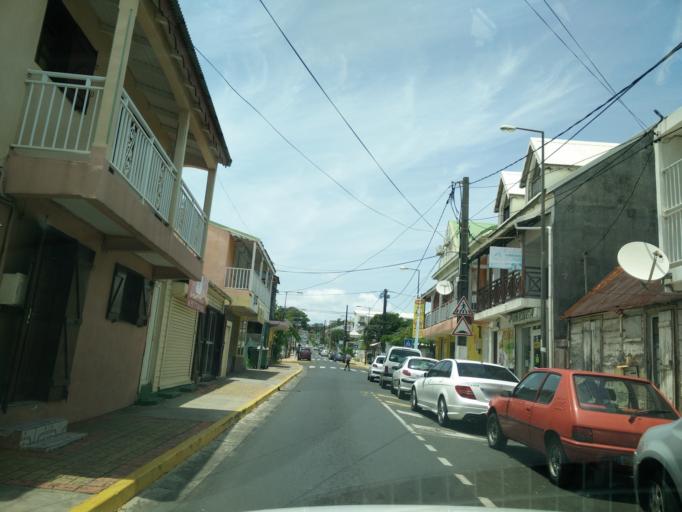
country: GP
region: Guadeloupe
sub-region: Guadeloupe
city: Petit-Bourg
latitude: 16.1935
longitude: -61.5914
